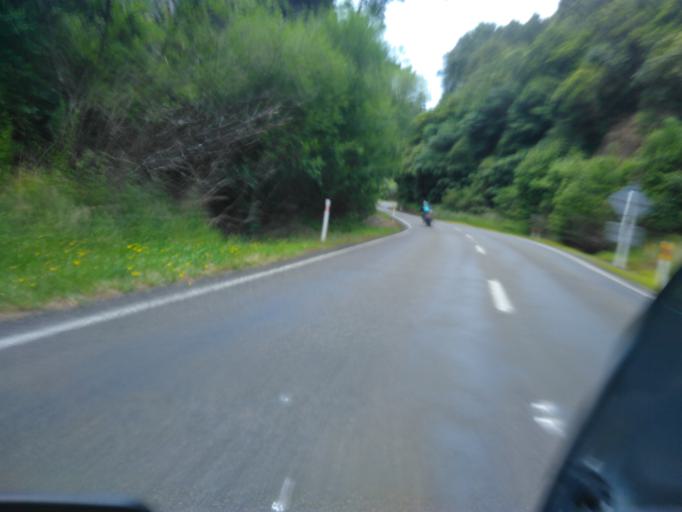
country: NZ
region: Bay of Plenty
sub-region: Opotiki District
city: Opotiki
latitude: -38.3408
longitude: 177.4380
